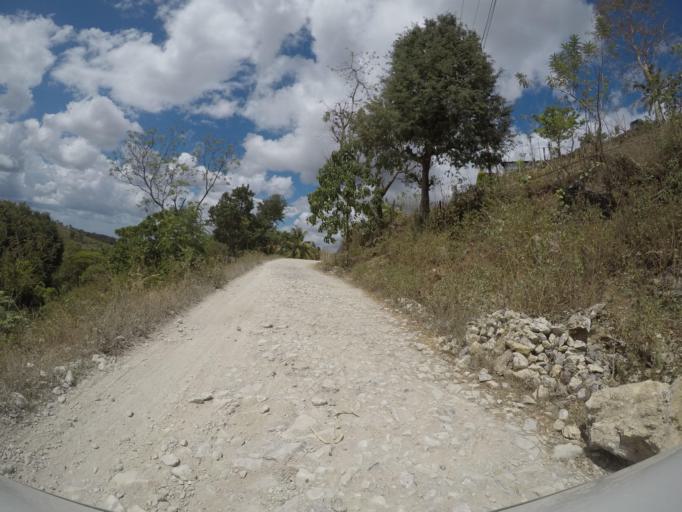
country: TL
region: Baucau
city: Baucau
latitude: -8.5276
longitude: 126.6960
